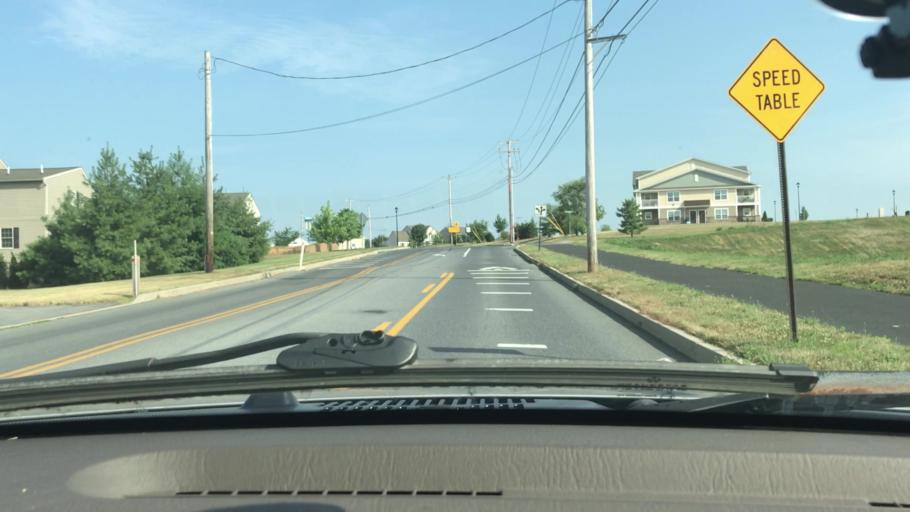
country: US
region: Pennsylvania
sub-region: Lancaster County
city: Rheems
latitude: 40.1408
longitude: -76.5648
